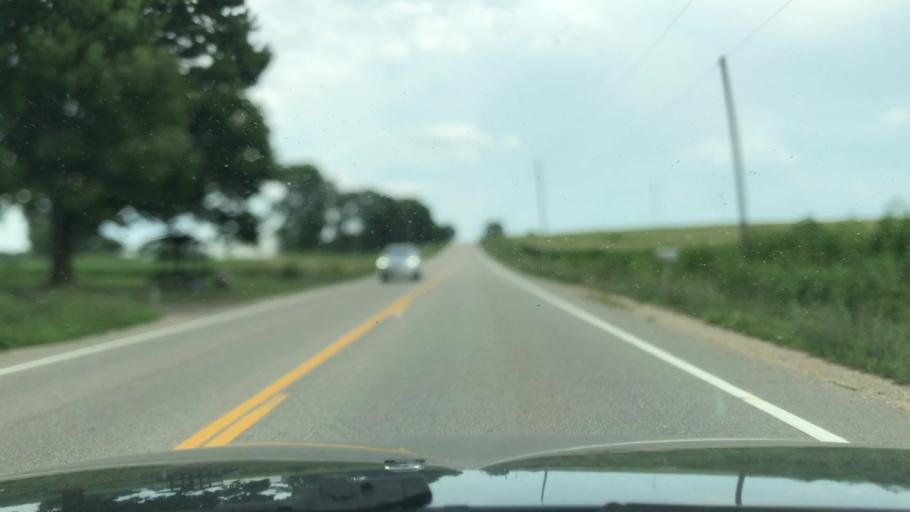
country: US
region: Michigan
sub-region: Ottawa County
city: Hudsonville
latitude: 42.8112
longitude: -85.8380
